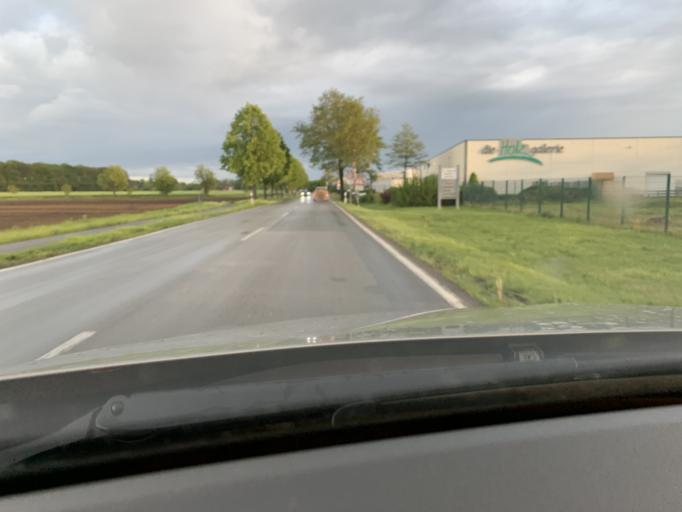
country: DE
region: North Rhine-Westphalia
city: Rietberg
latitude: 51.7659
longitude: 8.3855
